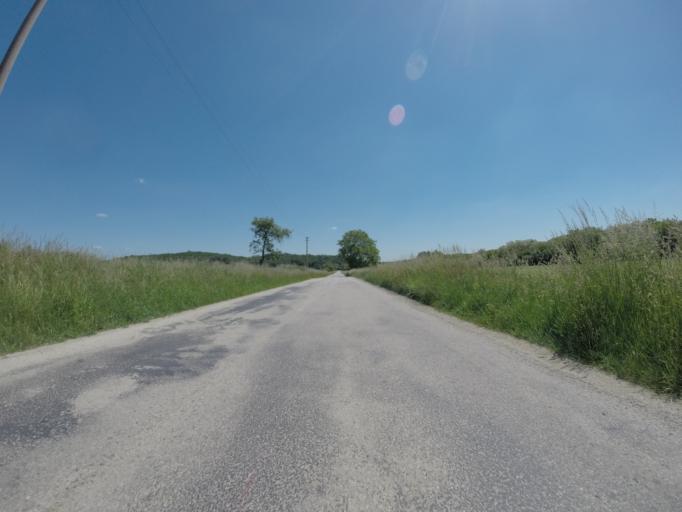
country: SK
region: Trnavsky
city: Hlohovec
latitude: 48.4867
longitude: 17.8841
